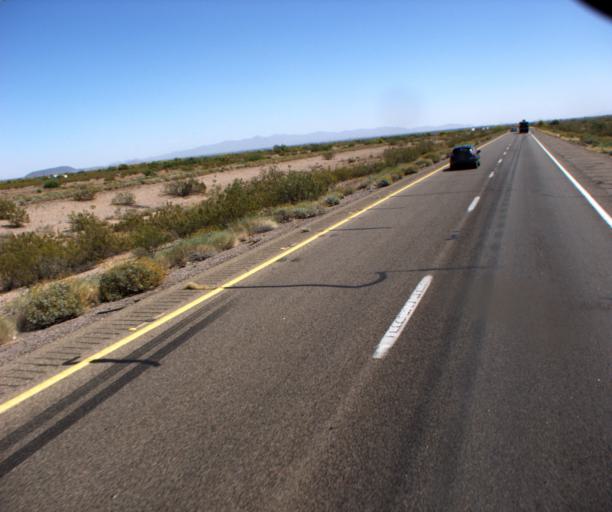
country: US
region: Arizona
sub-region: Maricopa County
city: Buckeye
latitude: 33.5034
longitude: -112.9701
